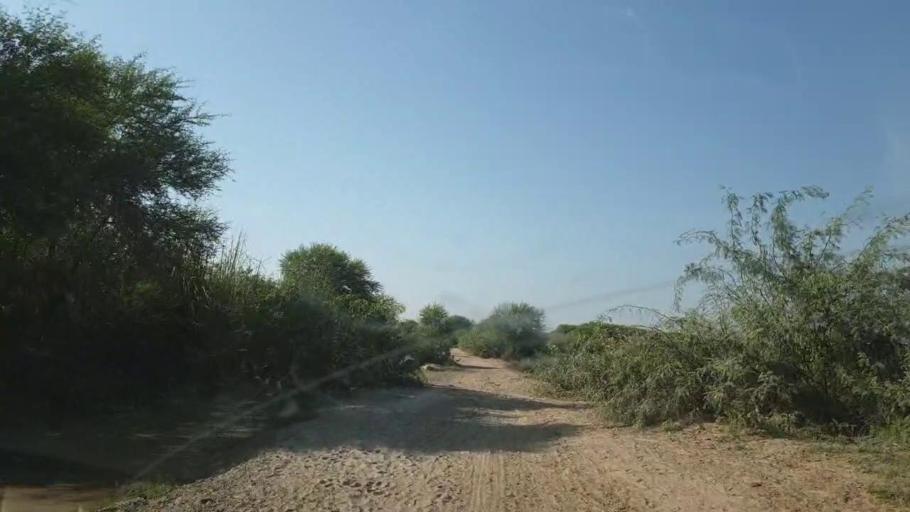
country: PK
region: Sindh
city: Tando Jam
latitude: 25.3494
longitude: 68.5716
